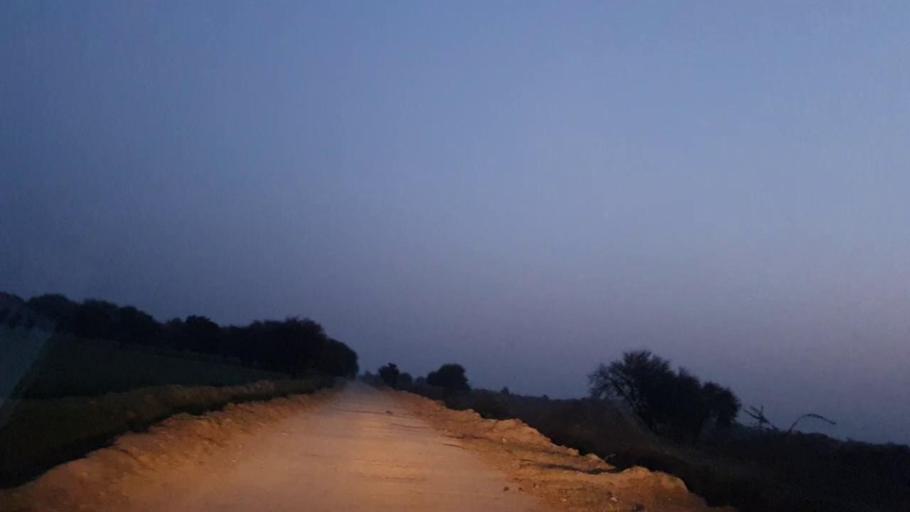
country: PK
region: Sindh
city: Tando Ghulam Ali
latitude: 25.0975
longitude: 68.9137
